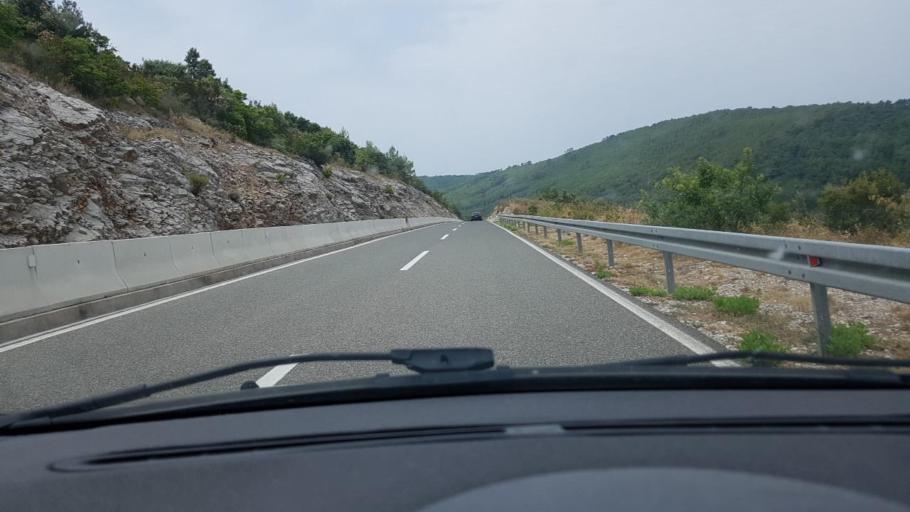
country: HR
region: Dubrovacko-Neretvanska
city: Smokvica
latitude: 42.9543
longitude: 16.9121
